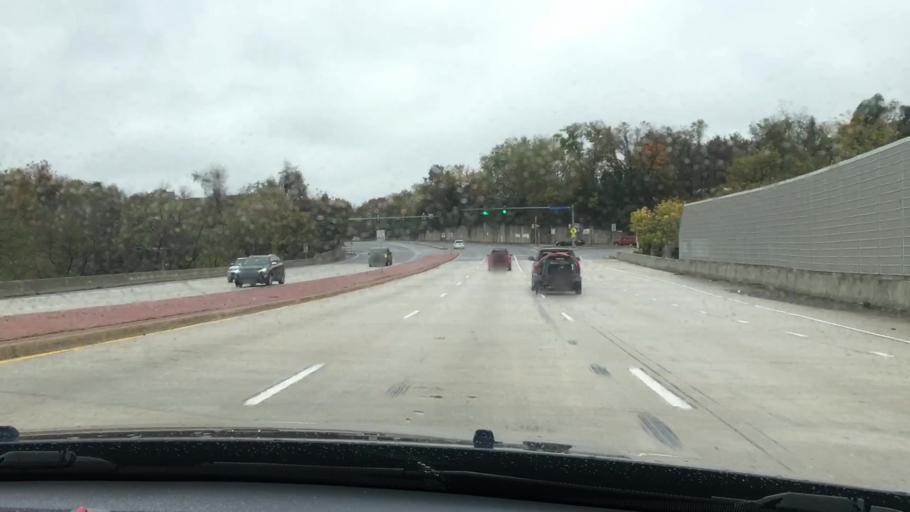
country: US
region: Virginia
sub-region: Prince William County
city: Woodbridge
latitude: 38.6826
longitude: -77.2584
